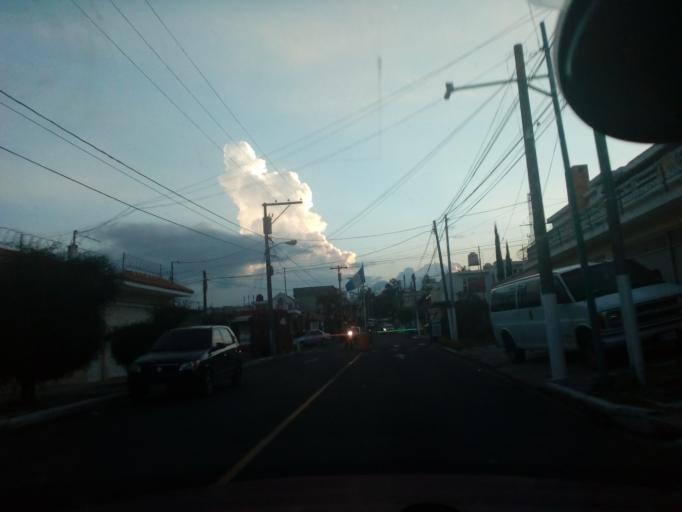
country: GT
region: Guatemala
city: Mixco
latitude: 14.6043
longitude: -90.5805
